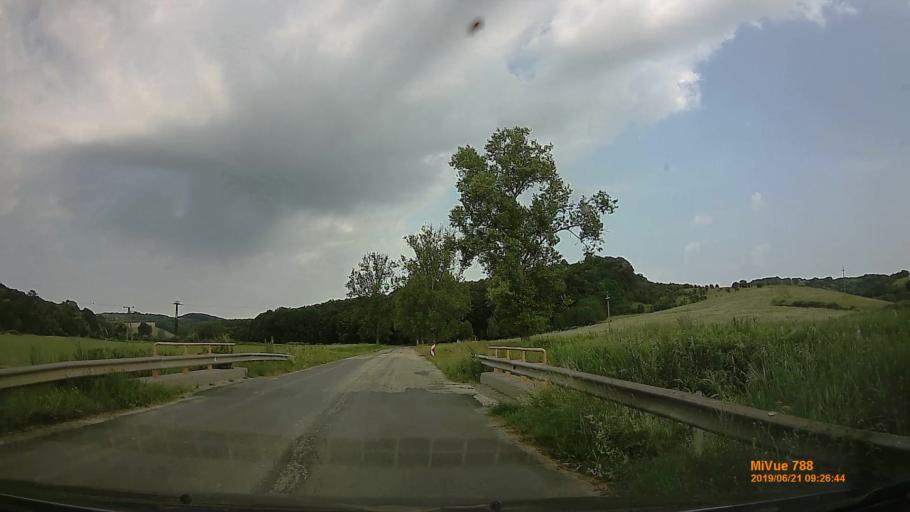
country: HU
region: Somogy
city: Taszar
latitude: 46.2737
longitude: 17.9031
